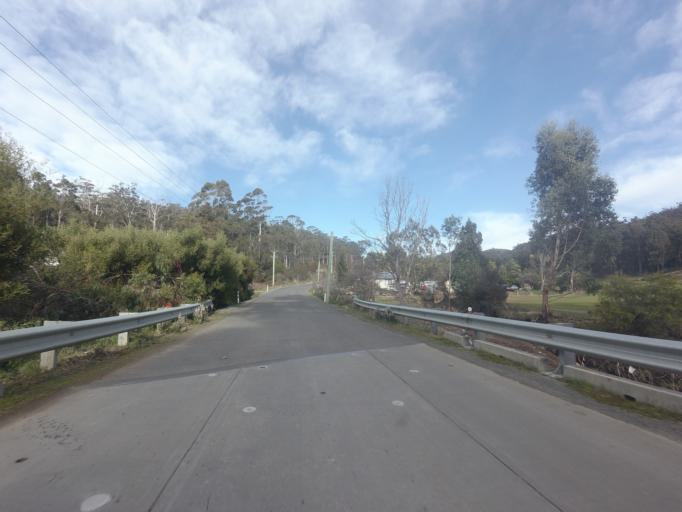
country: AU
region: Tasmania
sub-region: Kingborough
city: Margate
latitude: -42.9876
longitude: 147.1920
